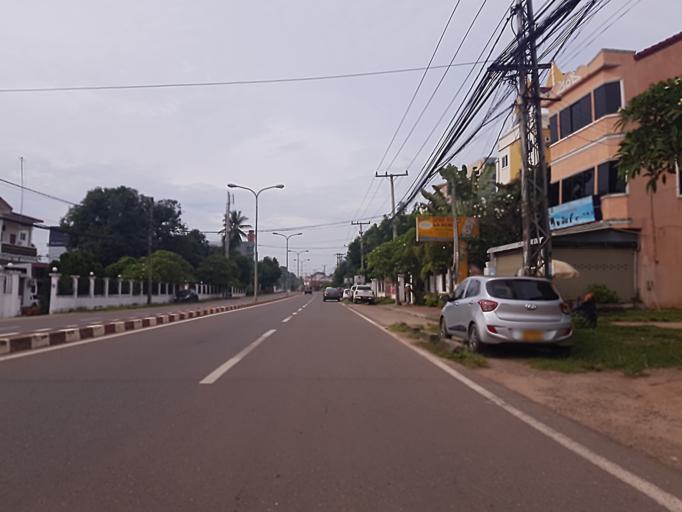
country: LA
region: Vientiane
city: Vientiane
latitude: 17.9447
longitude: 102.6194
